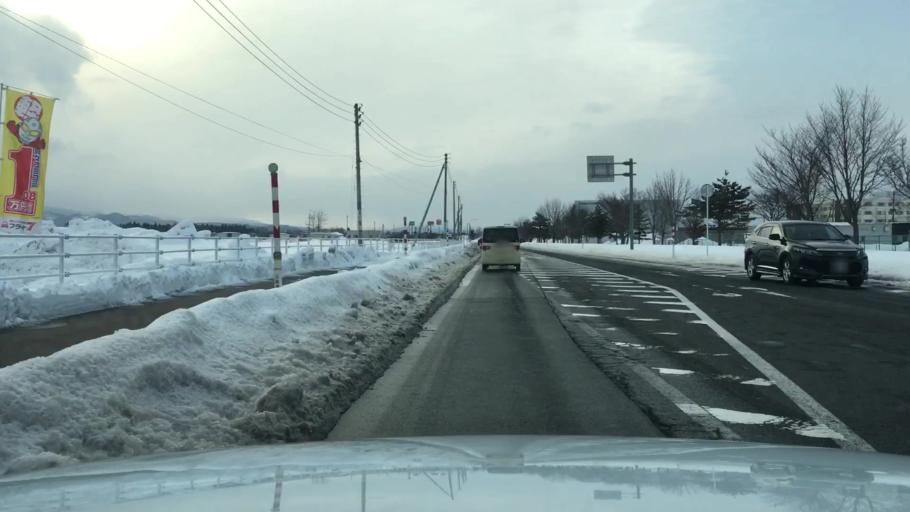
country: JP
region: Aomori
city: Hirosaki
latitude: 40.5854
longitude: 140.5071
